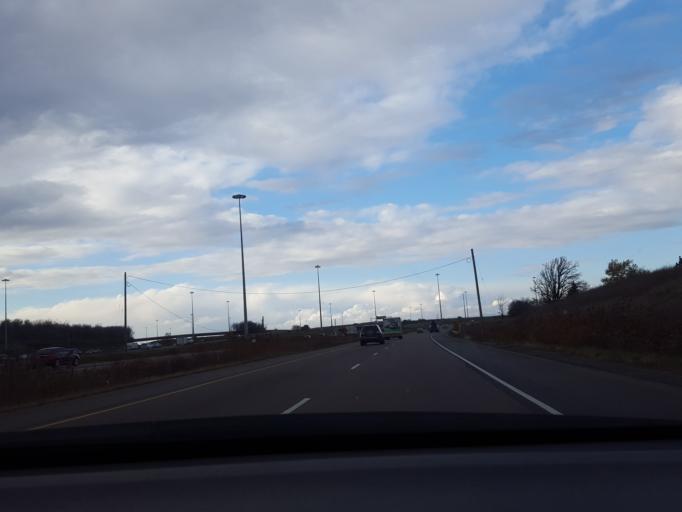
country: CA
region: Ontario
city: Mississauga
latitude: 43.6329
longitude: -79.6501
